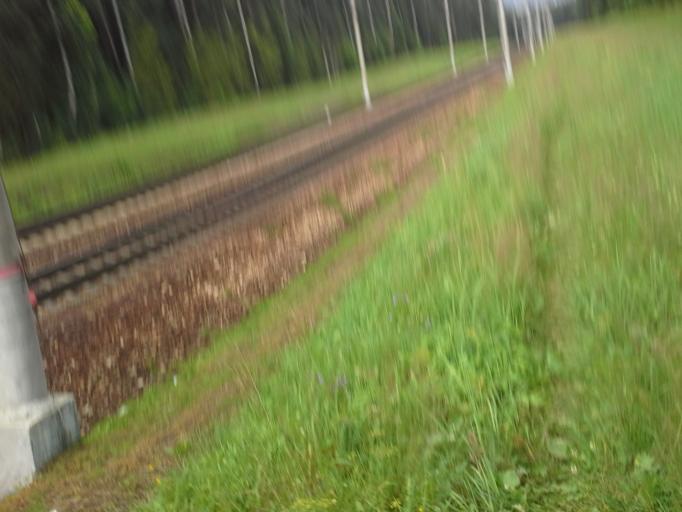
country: RU
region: Moskovskaya
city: Odintsovo
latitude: 55.6475
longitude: 37.2932
